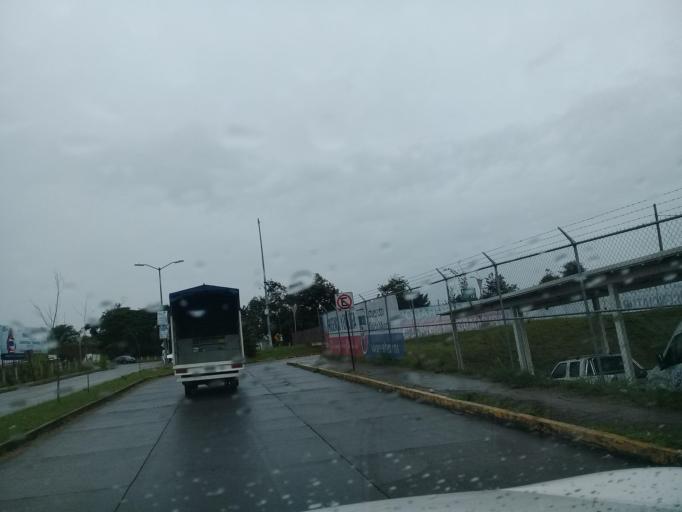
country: MX
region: Veracruz
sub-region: Emiliano Zapata
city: Las Trancas
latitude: 19.5041
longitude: -96.8561
